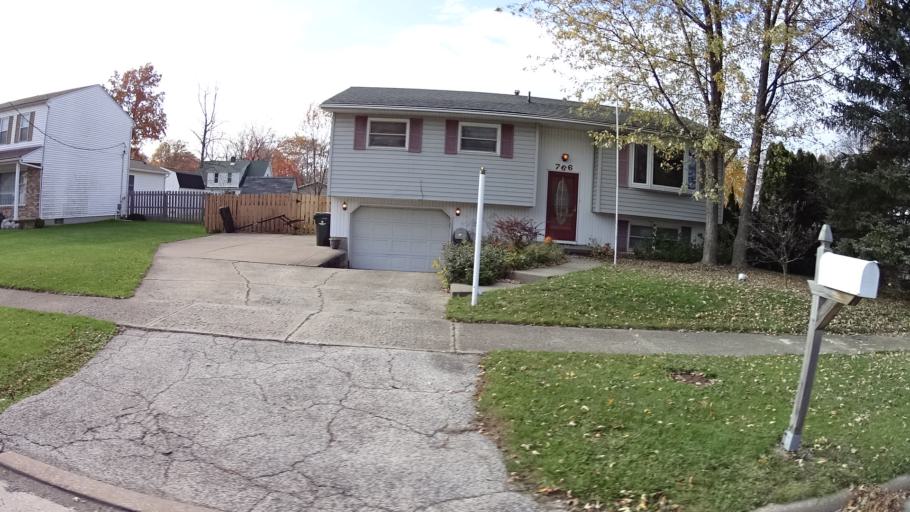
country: US
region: Ohio
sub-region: Lorain County
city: Sheffield Lake
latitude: 41.4858
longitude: -82.0946
